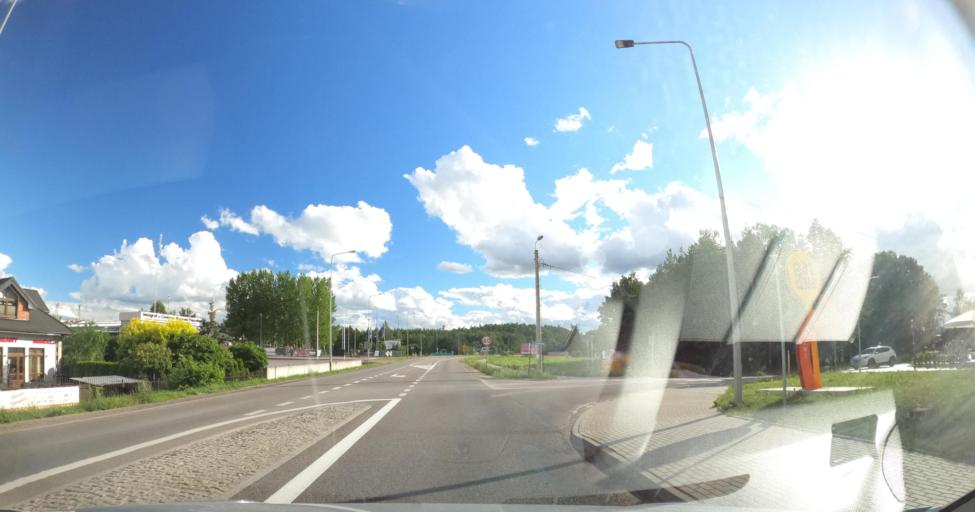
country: PL
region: Pomeranian Voivodeship
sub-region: Powiat kartuski
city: Zukowo
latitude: 54.3268
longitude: 18.3219
